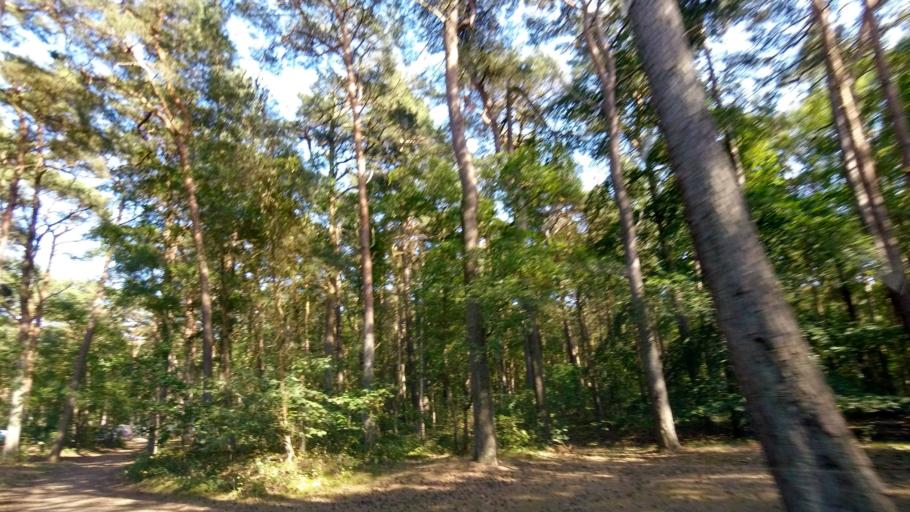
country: DE
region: Mecklenburg-Vorpommern
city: Wiek
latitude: 54.6718
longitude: 13.3011
